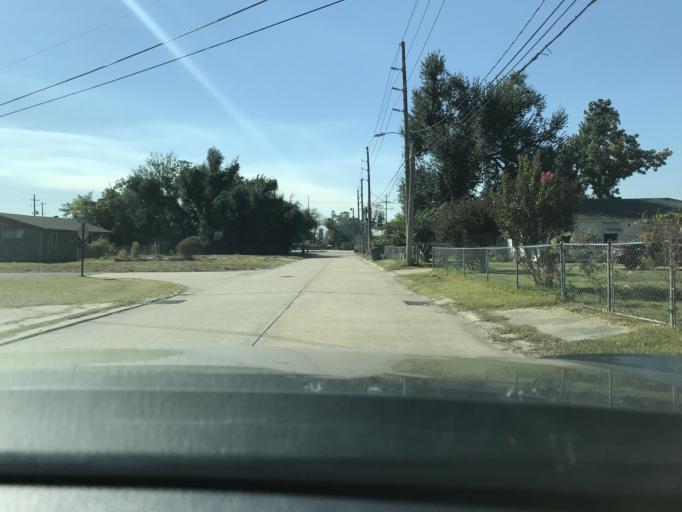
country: US
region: Louisiana
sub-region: Calcasieu Parish
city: Westlake
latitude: 30.2440
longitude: -93.2566
